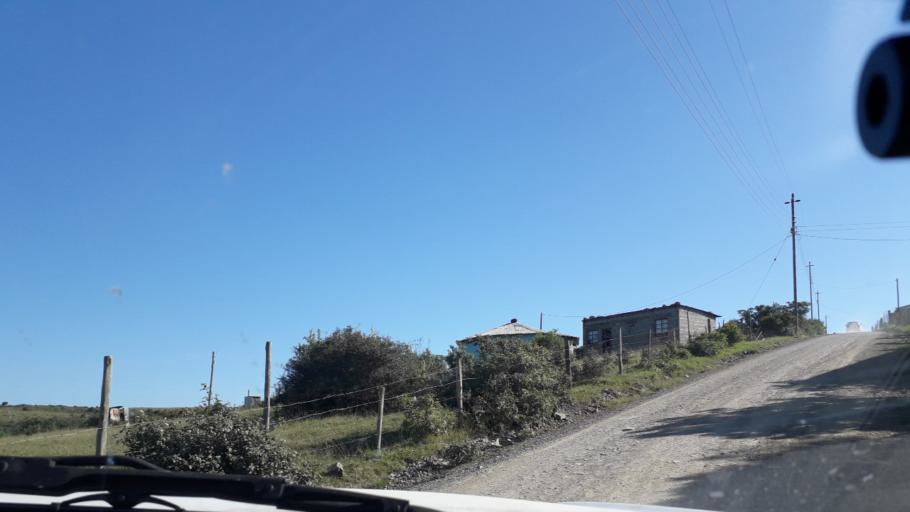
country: ZA
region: Eastern Cape
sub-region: Buffalo City Metropolitan Municipality
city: East London
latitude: -32.7999
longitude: 27.9614
